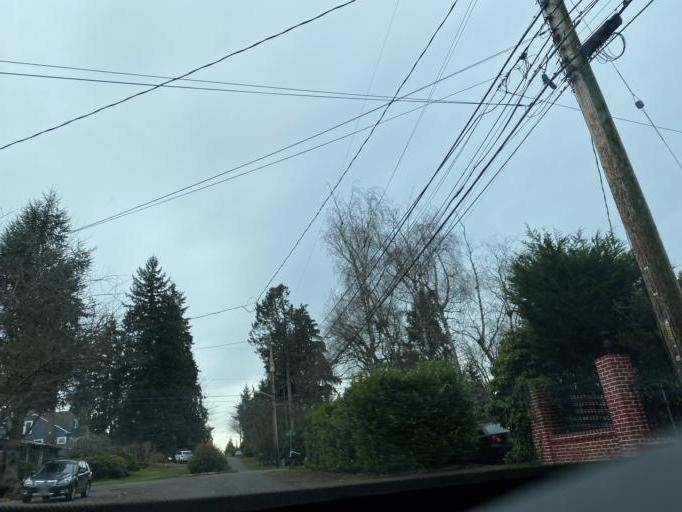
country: US
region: Washington
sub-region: King County
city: Lake Forest Park
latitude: 47.6966
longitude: -122.2926
